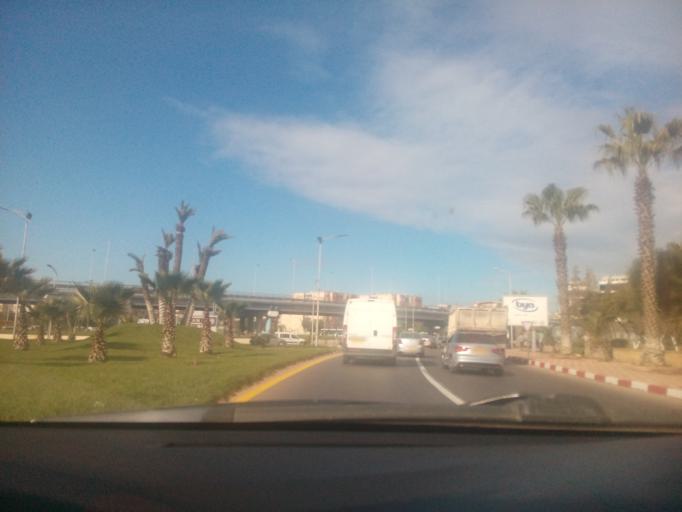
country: DZ
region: Oran
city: Oran
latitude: 35.6833
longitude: -0.6091
